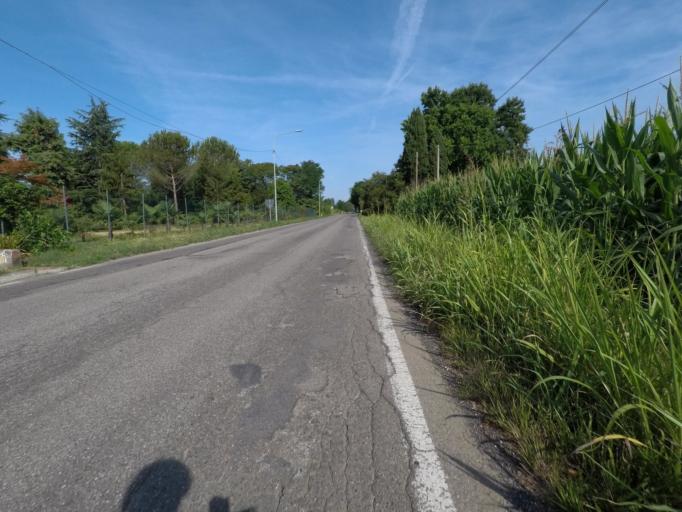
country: IT
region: Friuli Venezia Giulia
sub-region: Provincia di Udine
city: Colloredo di Prato
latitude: 46.0494
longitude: 13.1328
